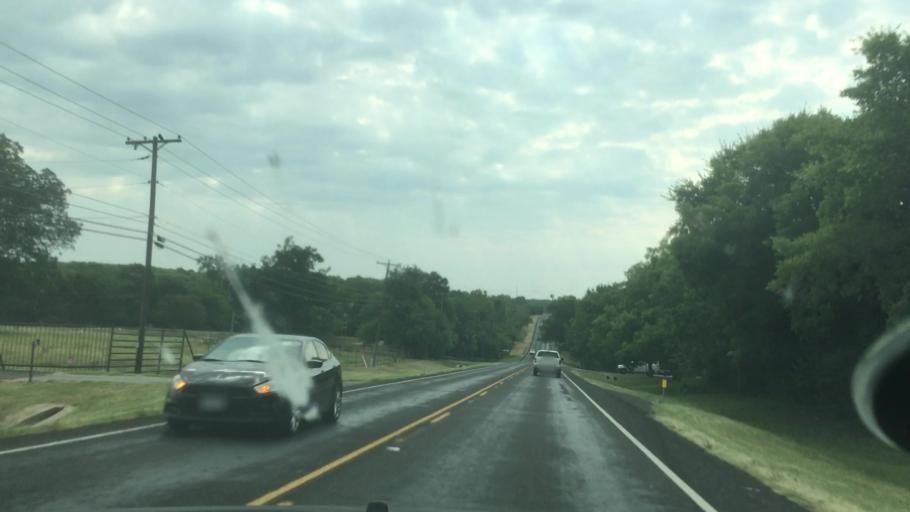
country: US
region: Texas
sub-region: Grayson County
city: Denison
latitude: 33.7850
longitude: -96.5972
